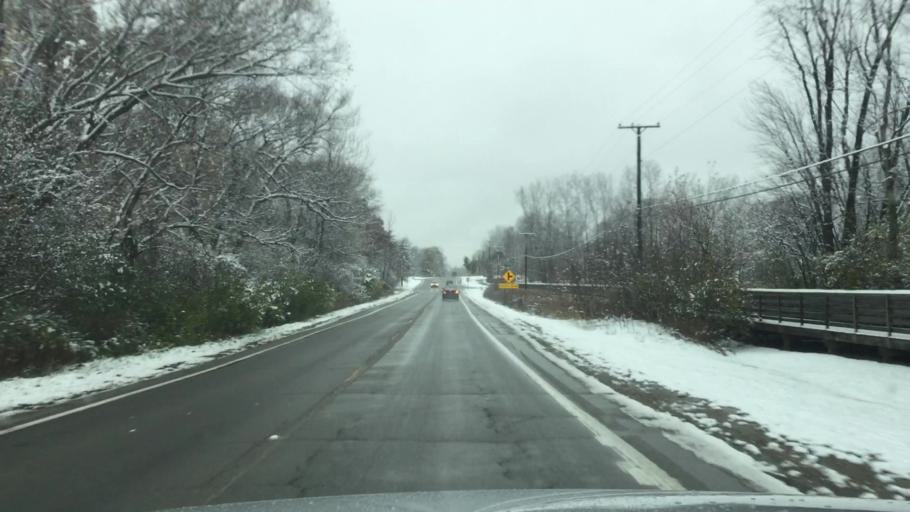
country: US
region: Michigan
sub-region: Oakland County
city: Oxford
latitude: 42.8101
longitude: -83.2638
